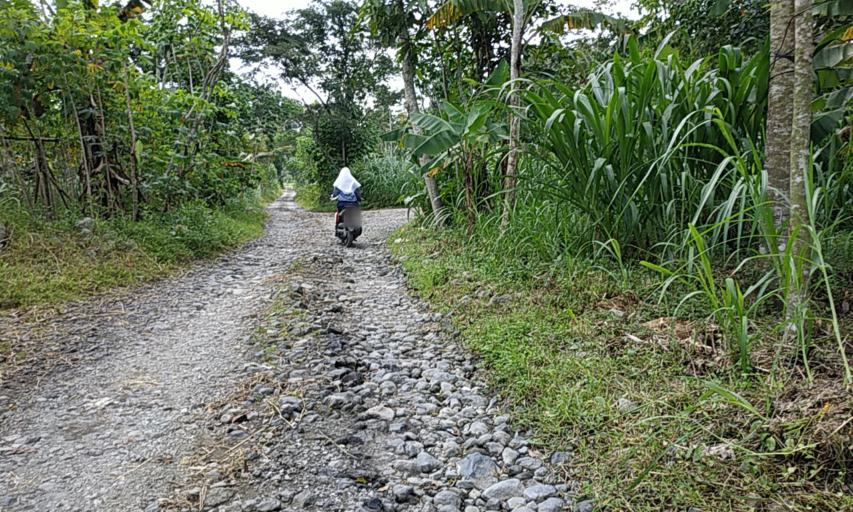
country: ID
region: Central Java
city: Jogonalan
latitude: -7.6337
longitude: 110.4871
